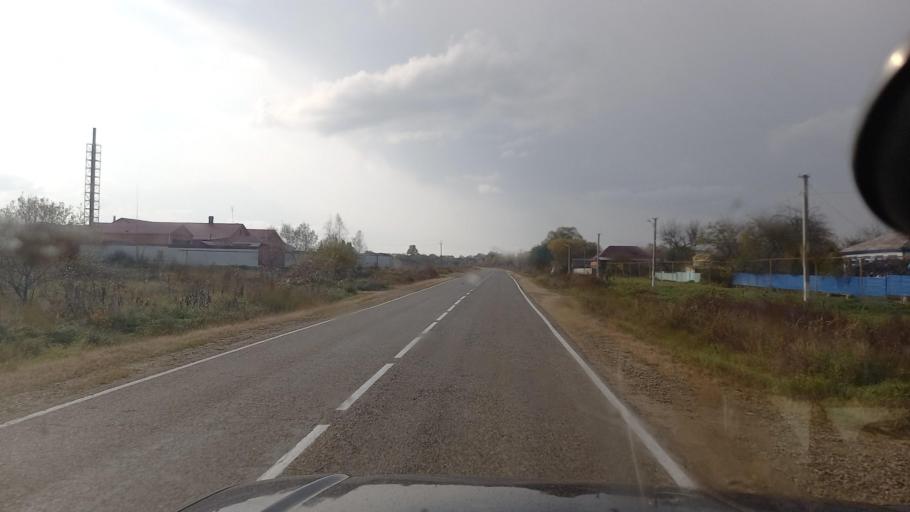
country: RU
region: Krasnodarskiy
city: Gubskaya
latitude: 44.3187
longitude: 40.6017
